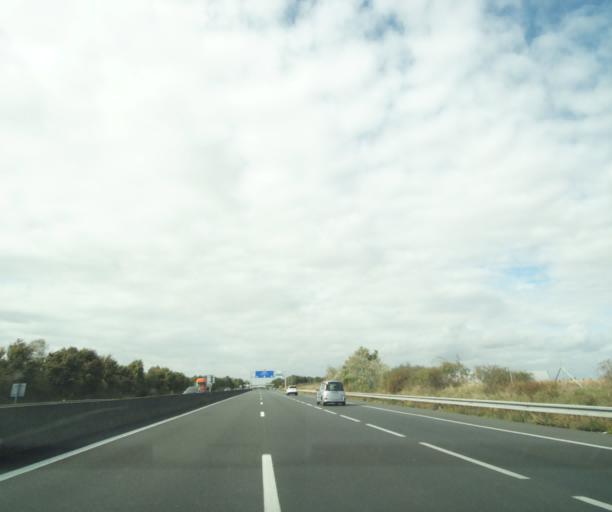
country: FR
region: Centre
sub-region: Departement d'Eure-et-Loir
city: Janville
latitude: 48.1986
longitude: 1.8511
